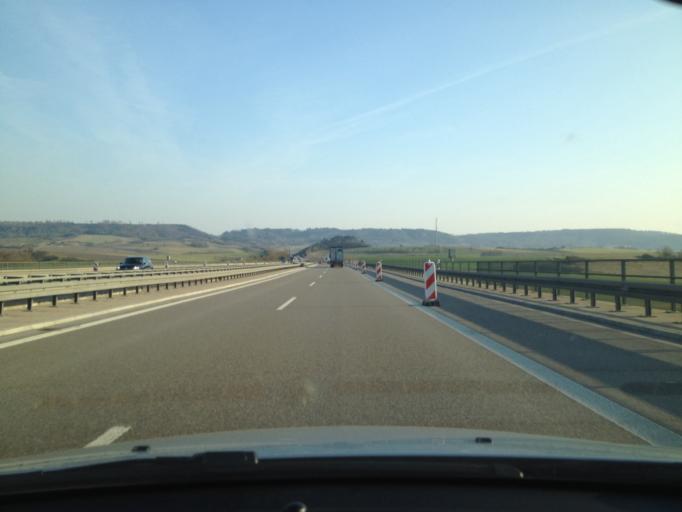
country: DE
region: Bavaria
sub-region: Regierungsbezirk Mittelfranken
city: Diebach
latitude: 49.3062
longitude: 10.2085
